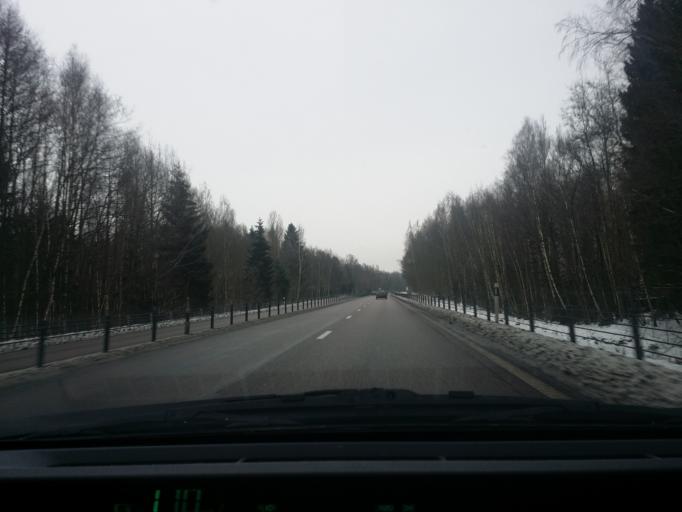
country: SE
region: Vaestra Goetaland
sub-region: Skovde Kommun
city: Stopen
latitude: 58.4946
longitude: 13.8468
